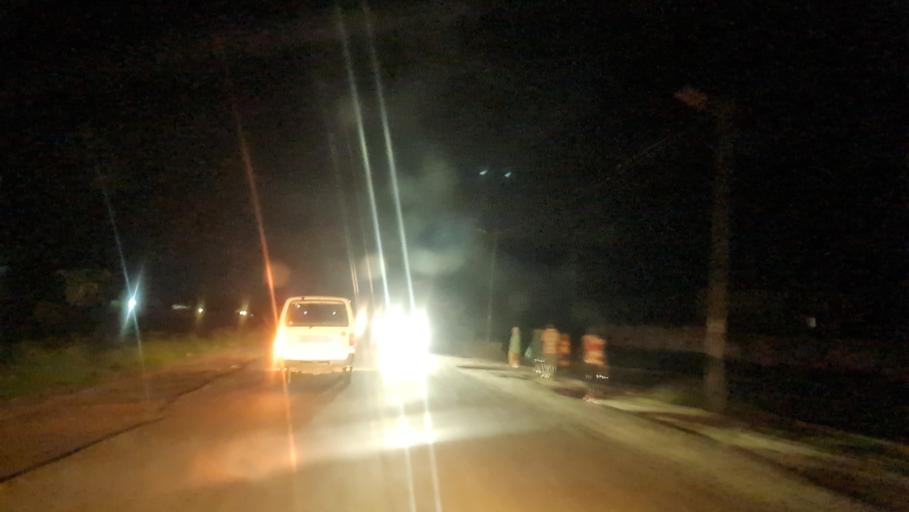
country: MZ
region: Nampula
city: Nacala
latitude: -14.6496
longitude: 40.6834
